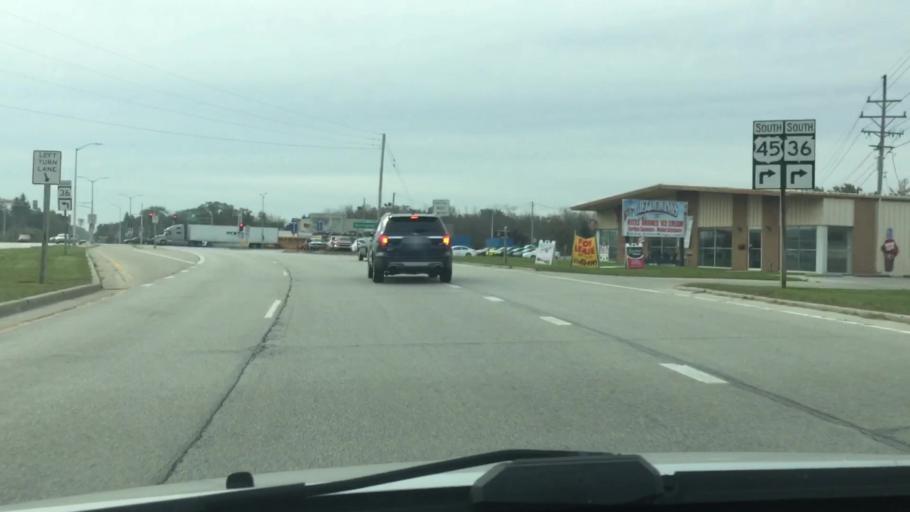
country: US
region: Wisconsin
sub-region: Milwaukee County
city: Franklin
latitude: 42.8903
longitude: -88.0393
